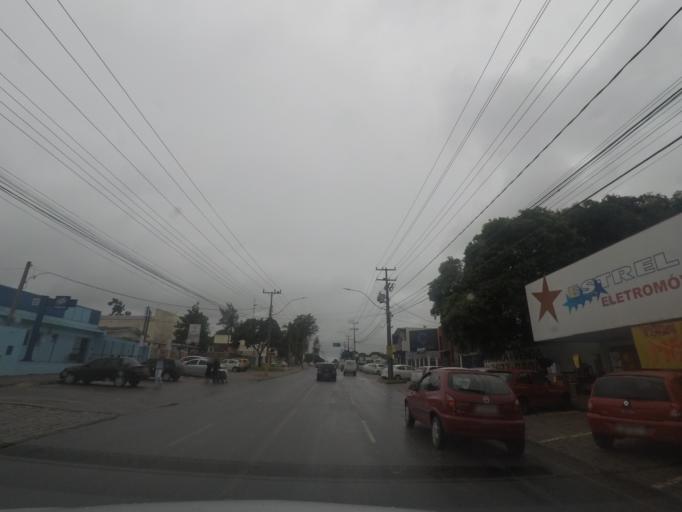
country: BR
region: Parana
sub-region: Piraquara
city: Piraquara
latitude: -25.4498
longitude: -49.0685
